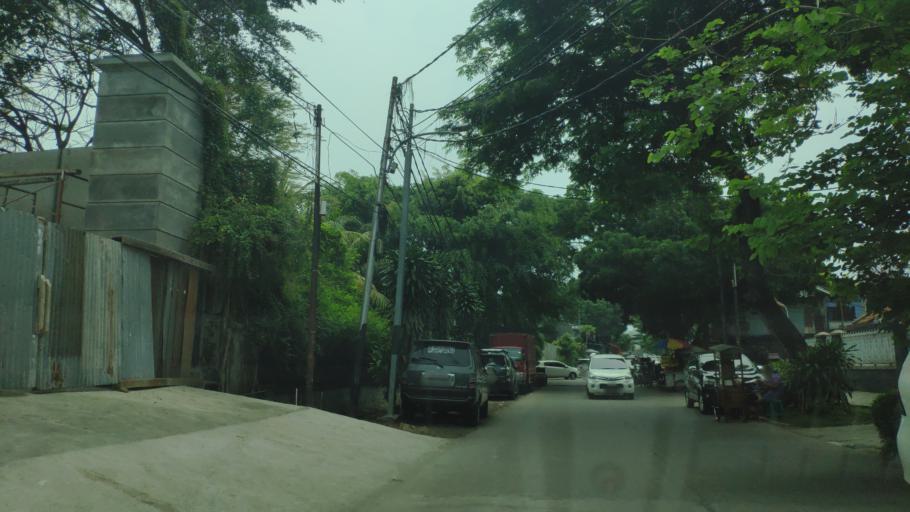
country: ID
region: Jakarta Raya
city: Jakarta
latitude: -6.1913
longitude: 106.8045
